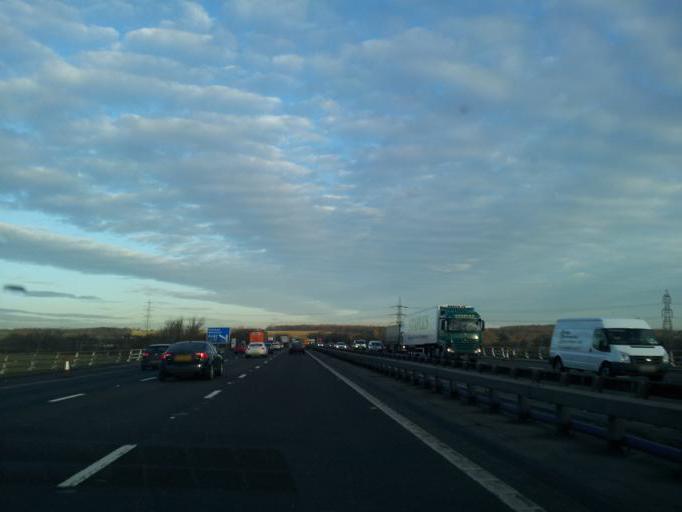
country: GB
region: England
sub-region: City and Borough of Wakefield
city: Normanton
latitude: 53.7212
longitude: -1.4278
